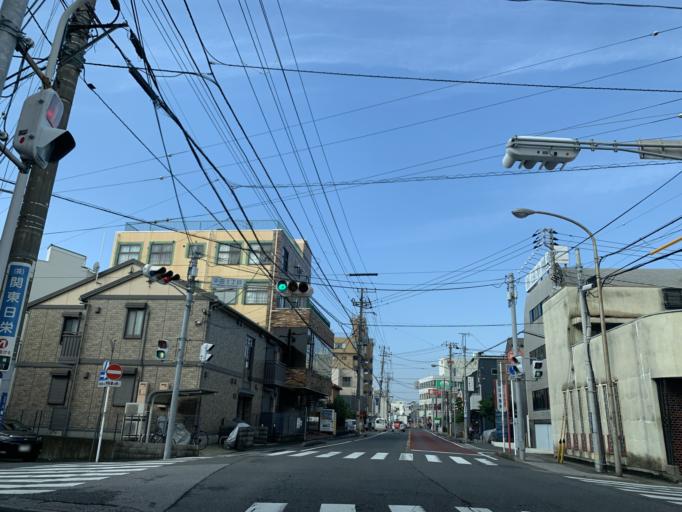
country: JP
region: Tokyo
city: Urayasu
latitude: 35.7238
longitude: 139.9232
